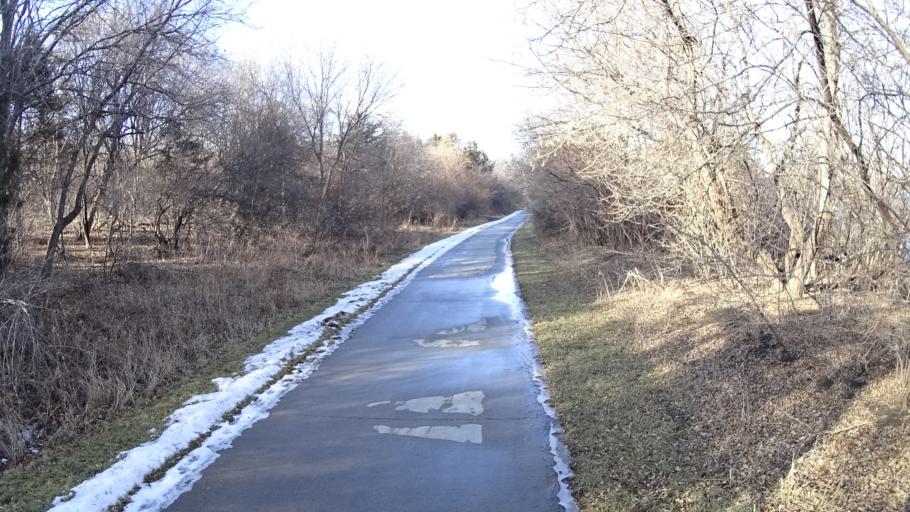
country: US
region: Nebraska
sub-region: Douglas County
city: Bennington
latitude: 41.3114
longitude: -96.1268
